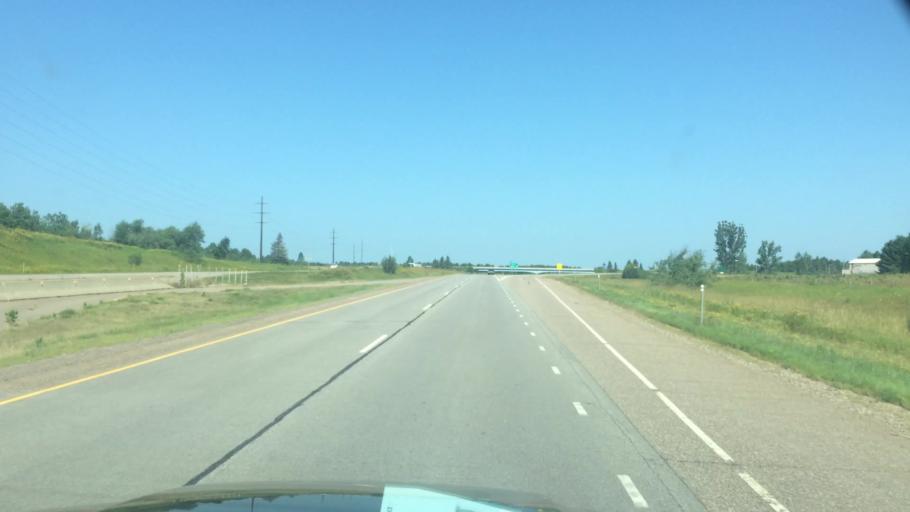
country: US
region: Wisconsin
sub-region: Lincoln County
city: Merrill
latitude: 45.2072
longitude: -89.6628
